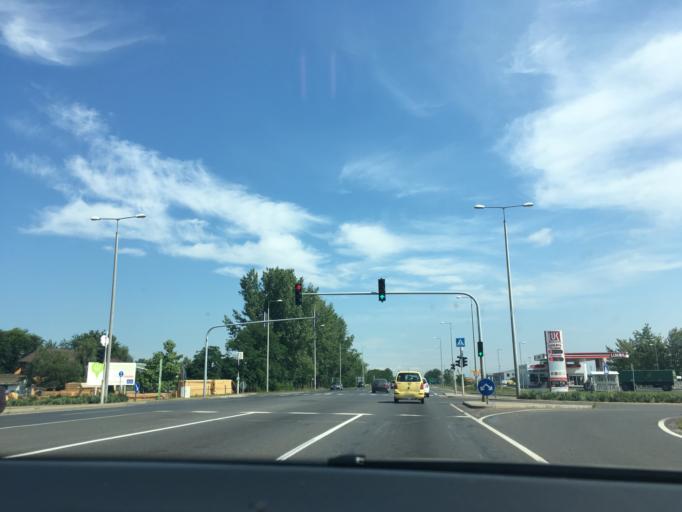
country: HU
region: Szabolcs-Szatmar-Bereg
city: Nyiregyhaza
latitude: 47.9012
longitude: 21.7118
